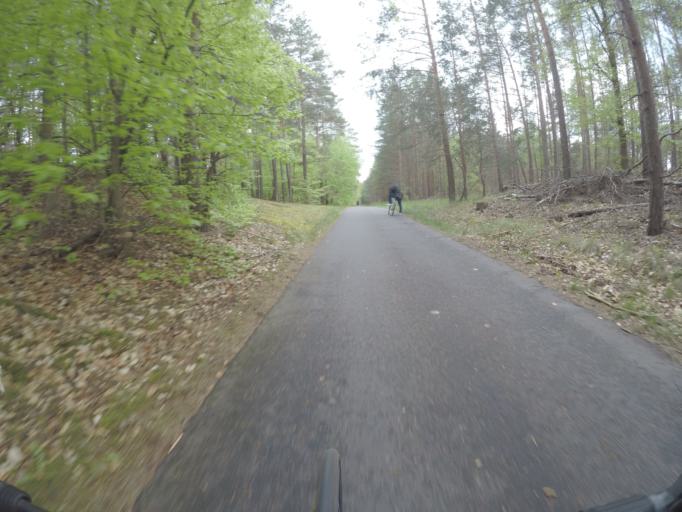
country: DE
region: Brandenburg
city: Biesenthal
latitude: 52.8095
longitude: 13.6329
